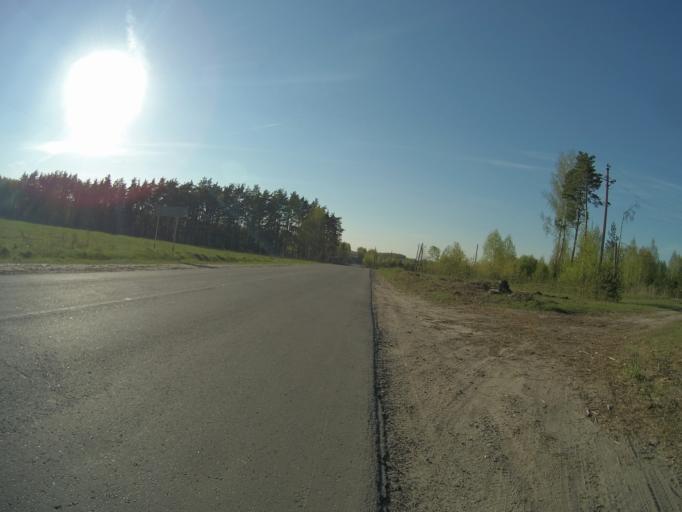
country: RU
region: Vladimir
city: Sudogda
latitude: 56.0601
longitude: 40.8142
